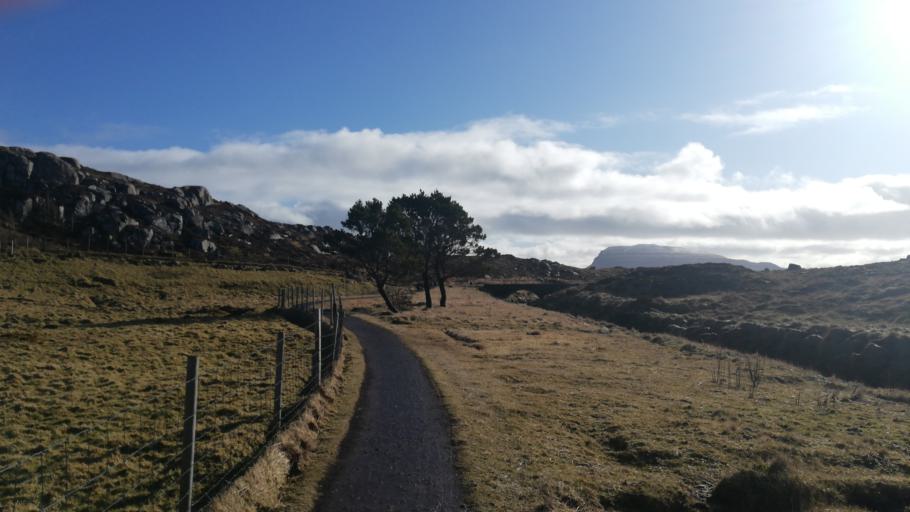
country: FO
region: Streymoy
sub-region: Torshavn
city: Torshavn
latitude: 62.0258
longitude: -6.7621
